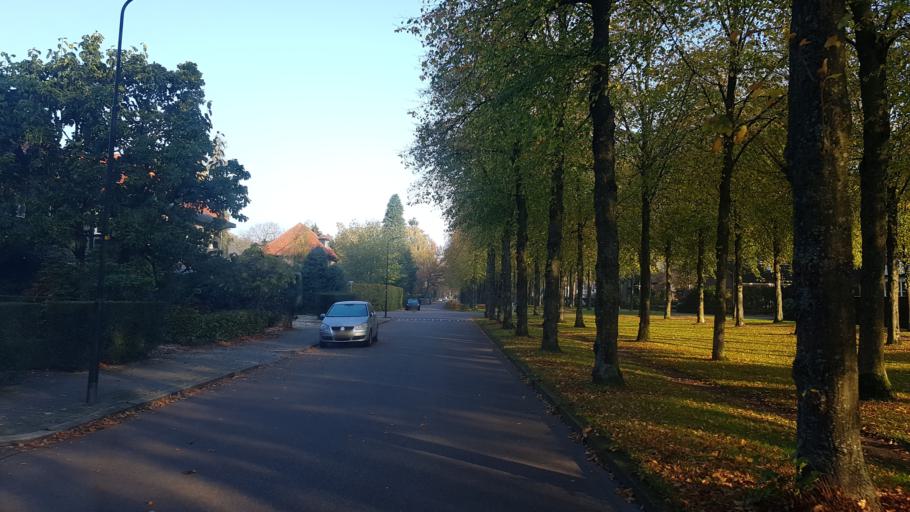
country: NL
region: Gelderland
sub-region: Gemeente Apeldoorn
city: Apeldoorn
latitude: 52.2225
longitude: 5.9461
